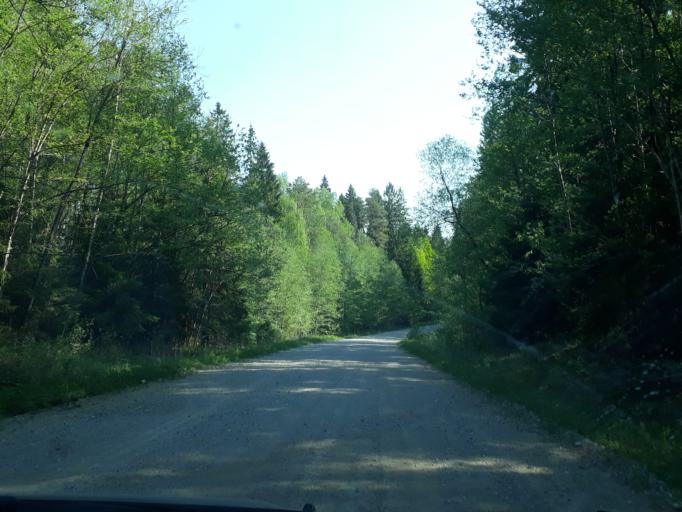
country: LV
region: Ligatne
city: Ligatne
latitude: 57.2797
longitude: 25.0777
